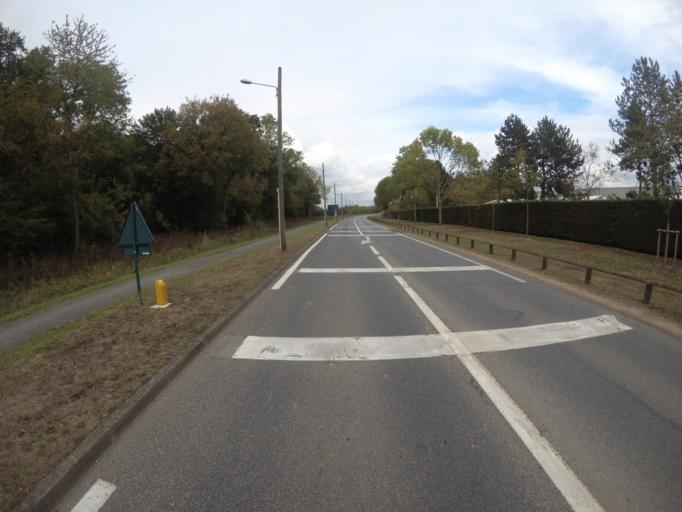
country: FR
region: Ile-de-France
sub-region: Departement de Seine-et-Marne
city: Montevrain
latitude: 48.8676
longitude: 2.7652
